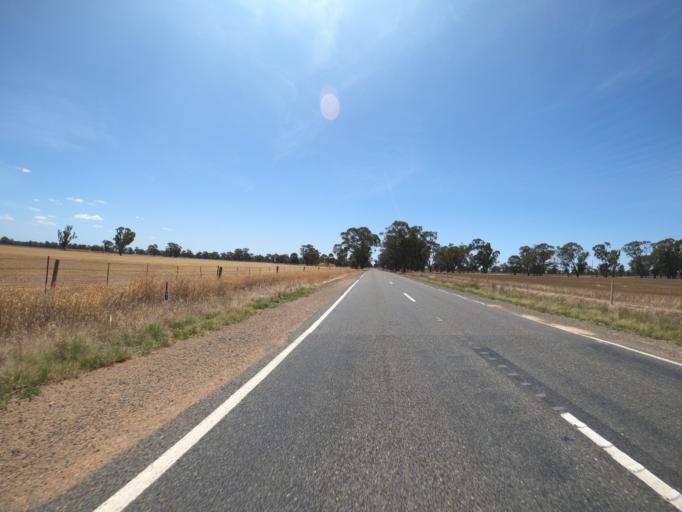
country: AU
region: Victoria
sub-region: Moira
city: Yarrawonga
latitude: -36.1856
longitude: 145.9672
